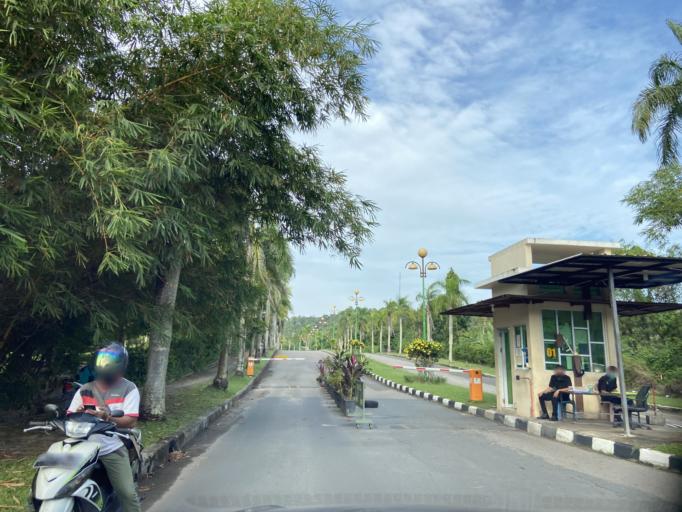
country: SG
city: Singapore
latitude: 1.1064
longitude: 104.0280
